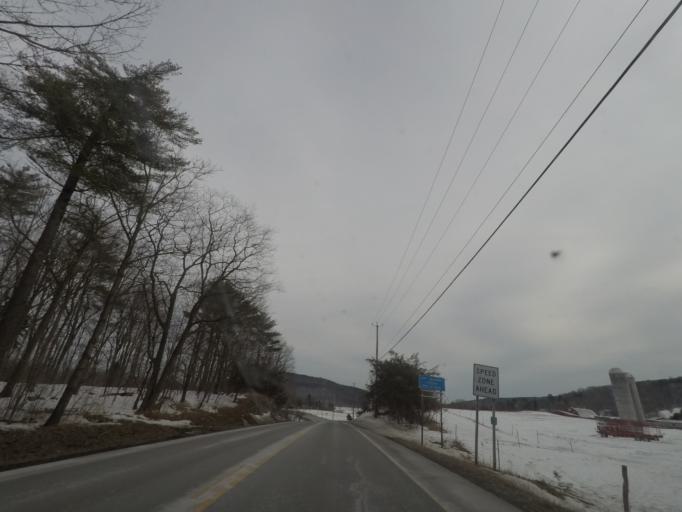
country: US
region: New York
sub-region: Albany County
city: Voorheesville
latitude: 42.5779
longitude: -73.9769
